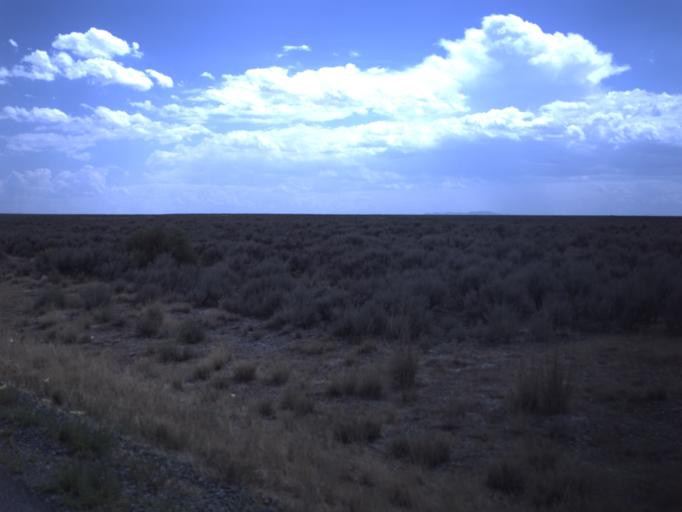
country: US
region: Utah
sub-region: Tooele County
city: Tooele
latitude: 40.3758
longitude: -112.3720
